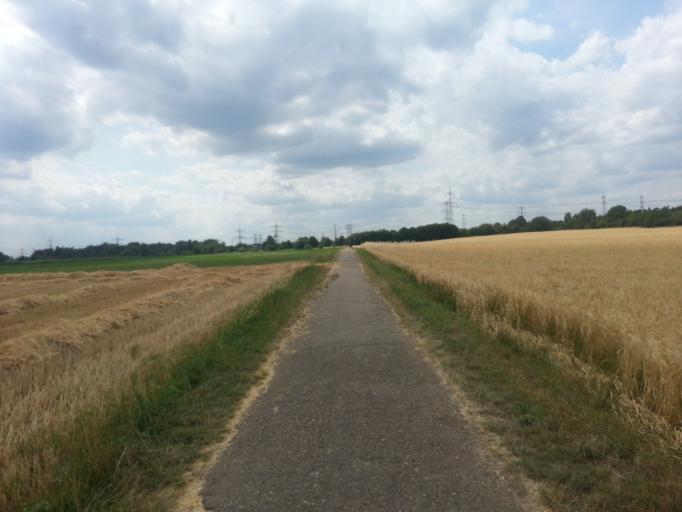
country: DE
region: Baden-Wuerttemberg
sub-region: Karlsruhe Region
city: Ilvesheim
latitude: 49.4884
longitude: 8.5663
